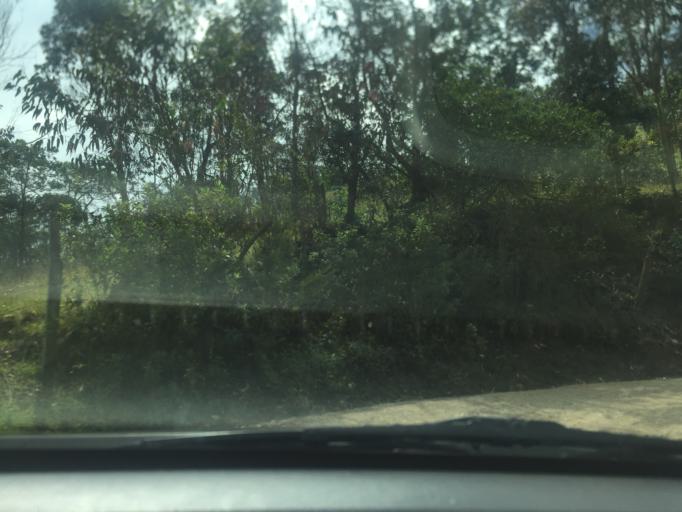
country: CO
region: Cundinamarca
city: Zipacon
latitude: 4.7850
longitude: -74.3785
